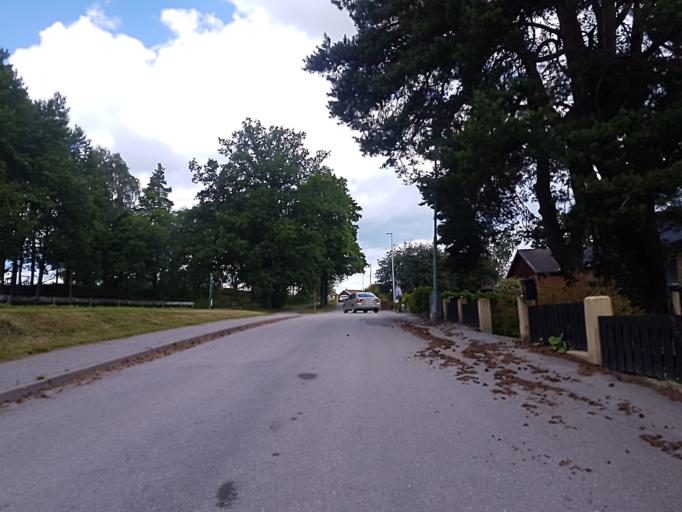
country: SE
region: Soedermanland
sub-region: Gnesta Kommun
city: Gnesta
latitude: 59.0454
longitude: 17.3190
